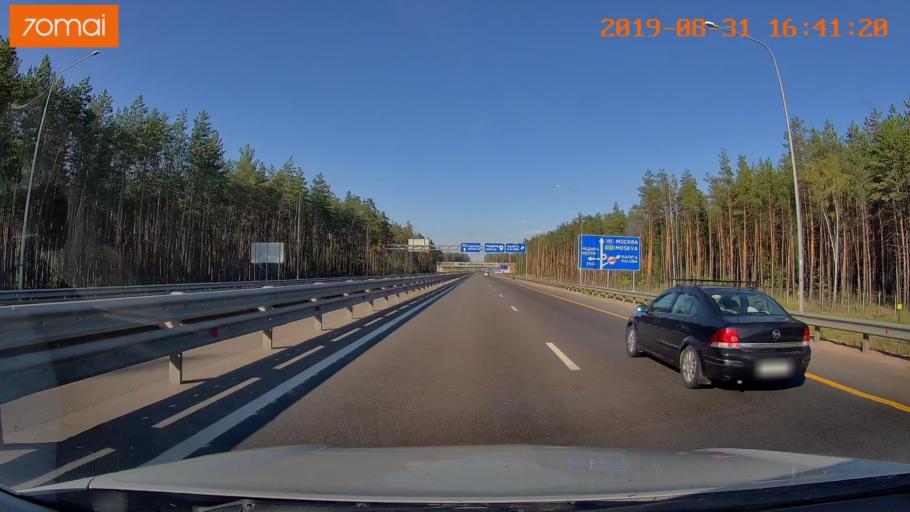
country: RU
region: Kaluga
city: Mstikhino
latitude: 54.5787
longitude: 36.0656
